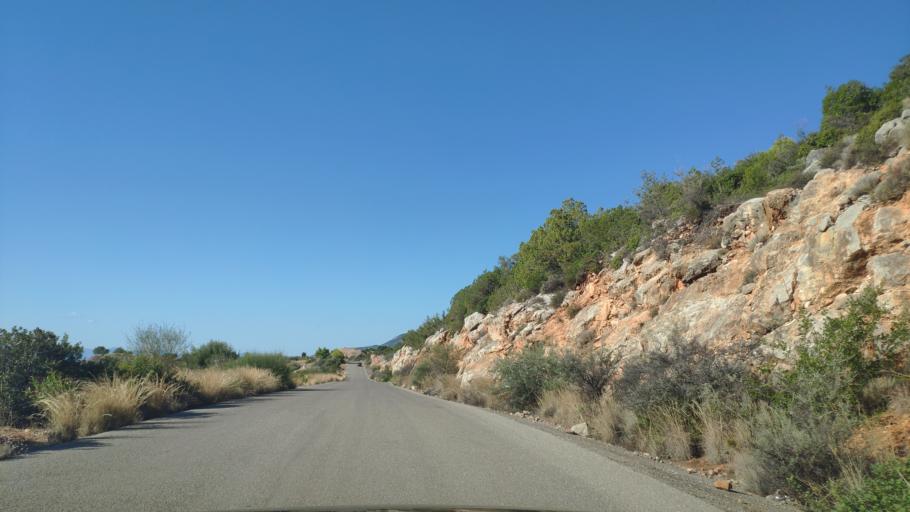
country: GR
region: Attica
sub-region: Nomos Piraios
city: Galatas
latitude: 37.5645
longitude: 23.3628
